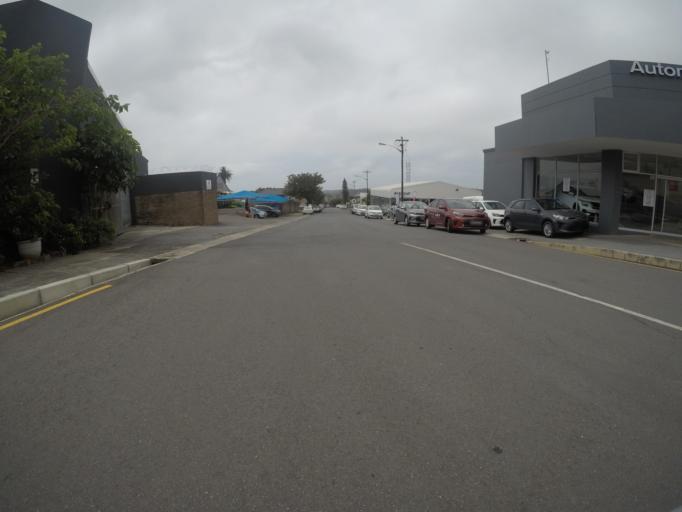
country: ZA
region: Eastern Cape
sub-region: Buffalo City Metropolitan Municipality
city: East London
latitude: -32.9862
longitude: 27.9202
